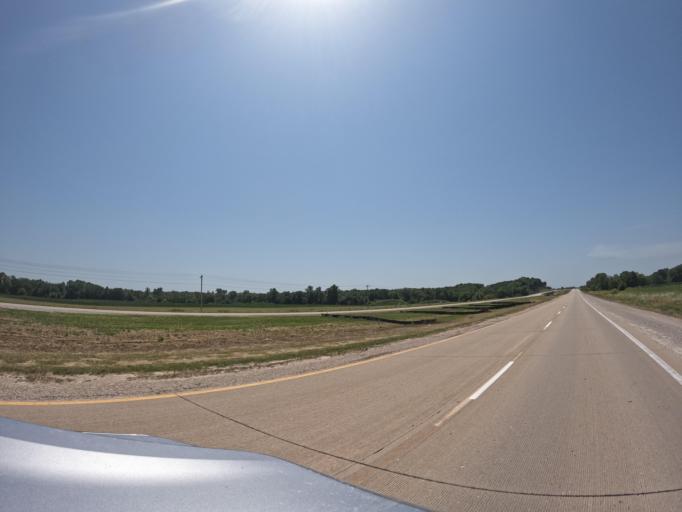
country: US
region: Iowa
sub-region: Henry County
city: Mount Pleasant
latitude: 40.9758
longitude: -91.6731
